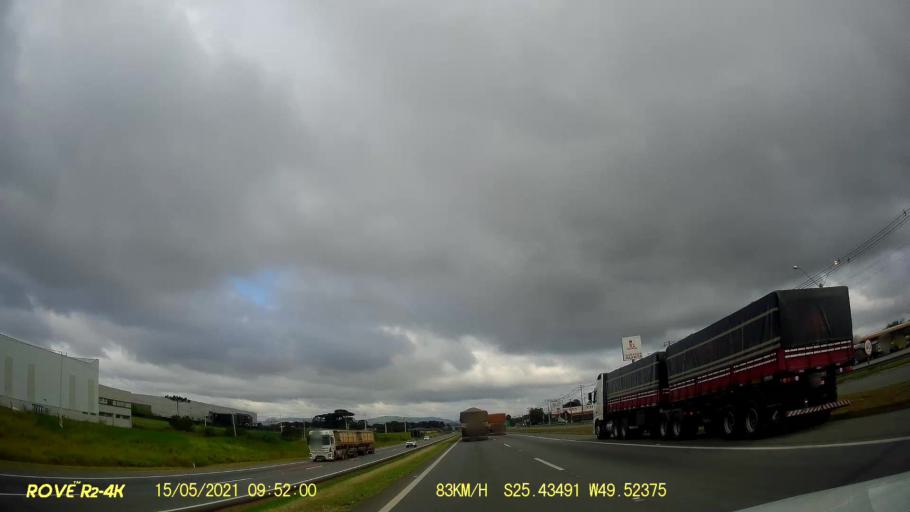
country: BR
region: Parana
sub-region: Campo Largo
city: Campo Largo
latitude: -25.4347
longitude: -49.5238
